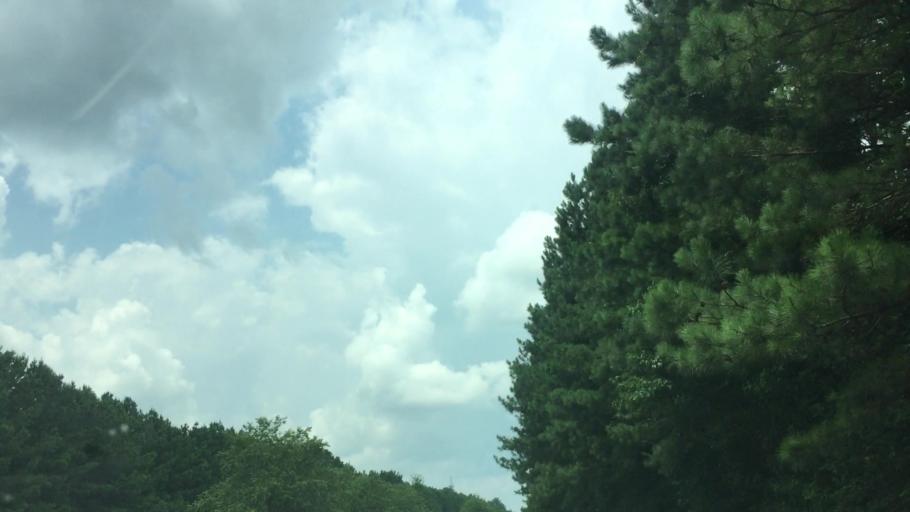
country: US
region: Georgia
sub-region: Fulton County
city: Union City
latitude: 33.6202
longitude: -84.5724
